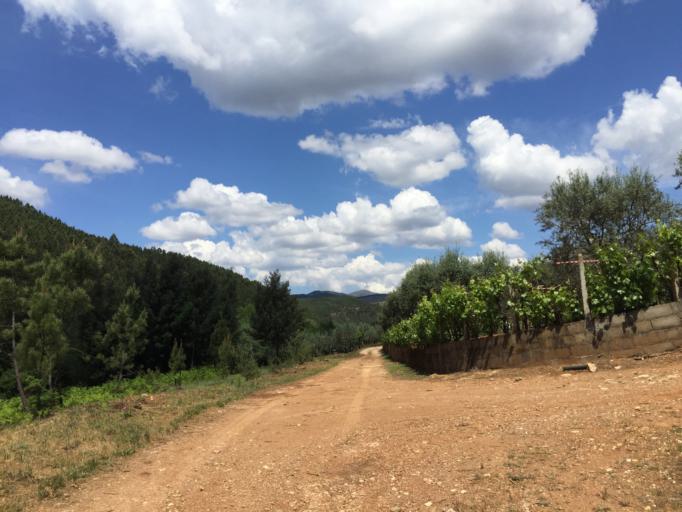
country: PT
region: Coimbra
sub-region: Pampilhosa da Serra
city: Pampilhosa da Serra
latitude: 40.0727
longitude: -7.7845
